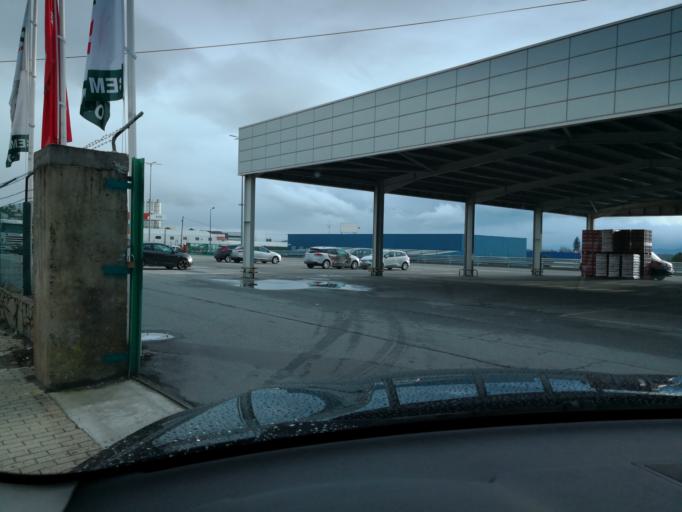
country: PT
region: Vila Real
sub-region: Vila Real
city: Vila Real
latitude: 41.2767
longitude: -7.7046
